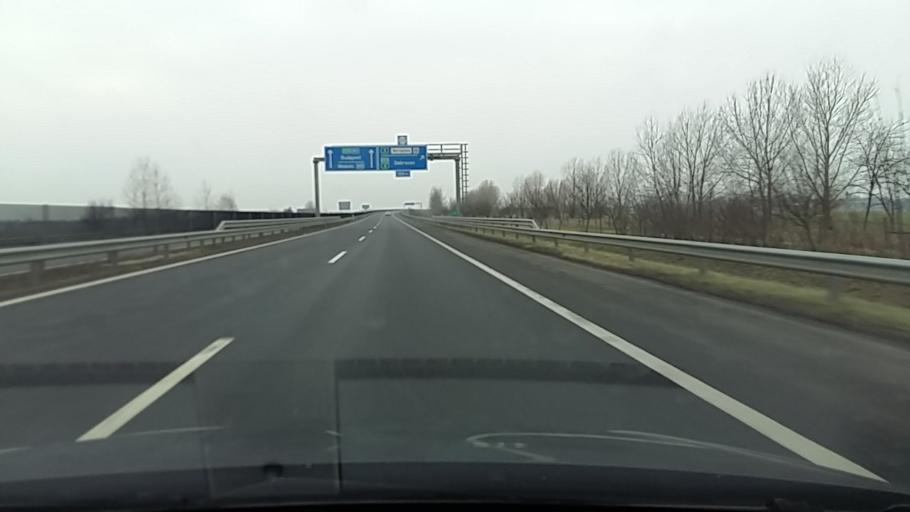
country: HU
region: Szabolcs-Szatmar-Bereg
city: Nyiregyhaza
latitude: 47.8855
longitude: 21.7291
